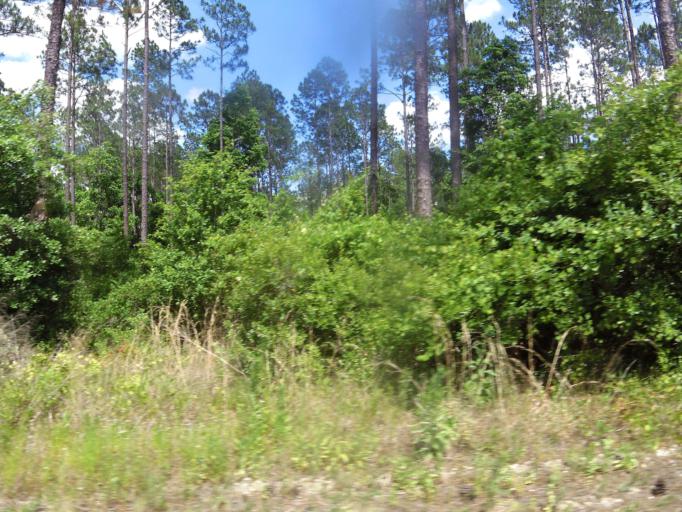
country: US
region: Florida
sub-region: Clay County
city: Asbury Lake
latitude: 29.8836
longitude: -81.8525
